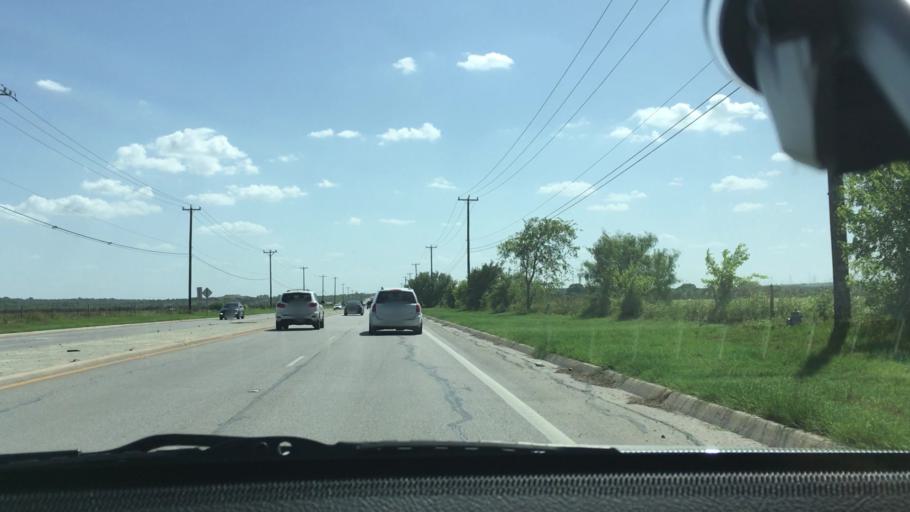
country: US
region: Texas
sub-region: Bexar County
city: Selma
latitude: 29.6038
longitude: -98.3289
